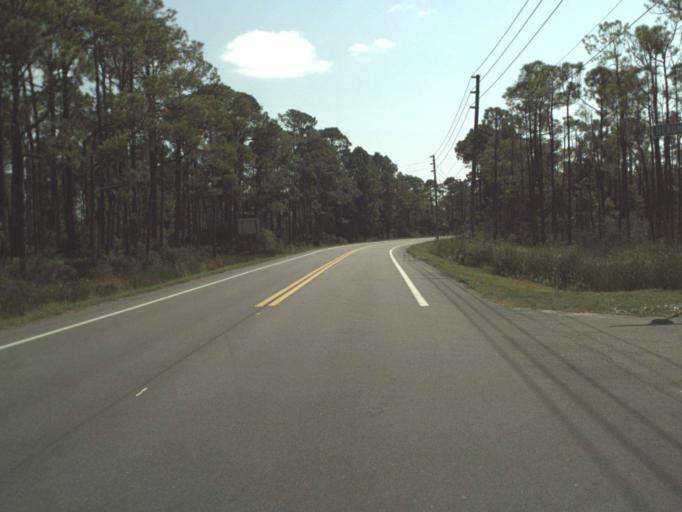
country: US
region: Florida
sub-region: Gulf County
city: Port Saint Joe
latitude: 29.7171
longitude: -85.3032
